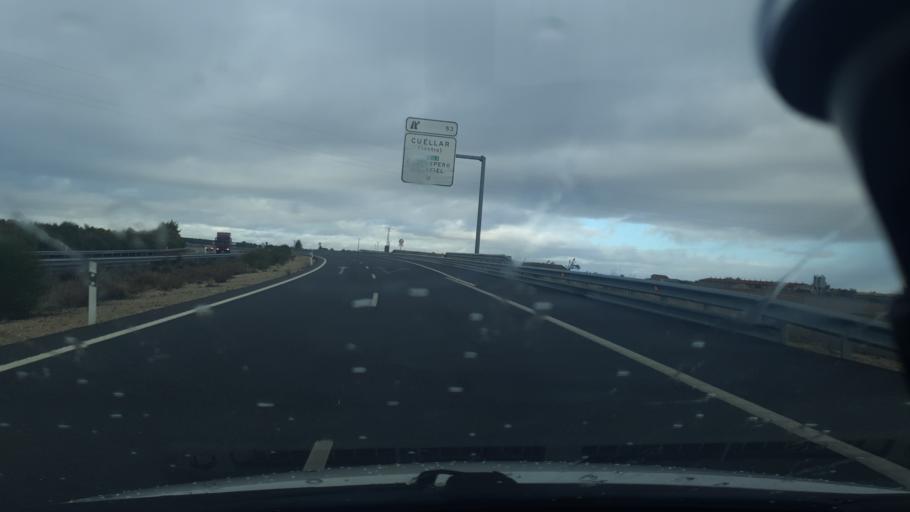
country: ES
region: Castille and Leon
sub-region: Provincia de Segovia
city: Cuellar
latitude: 41.4029
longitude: -4.2931
